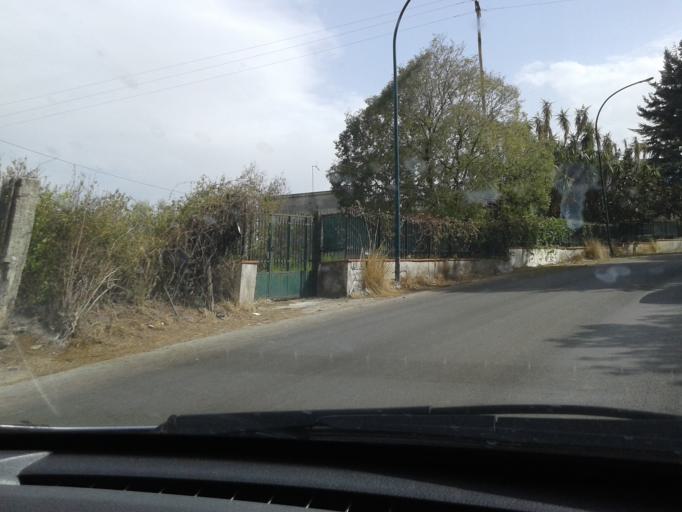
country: IT
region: Sicily
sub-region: Palermo
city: Cannizzaro-Favara
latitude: 38.0731
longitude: 13.2771
